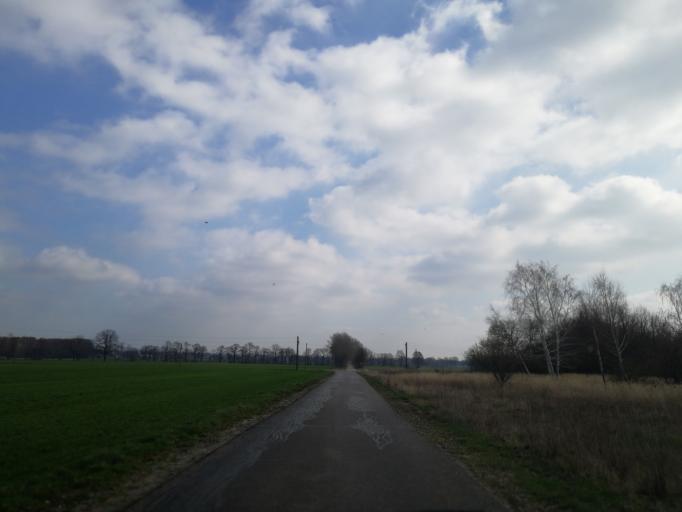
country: DE
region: Brandenburg
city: Finsterwalde
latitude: 51.6586
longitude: 13.7161
